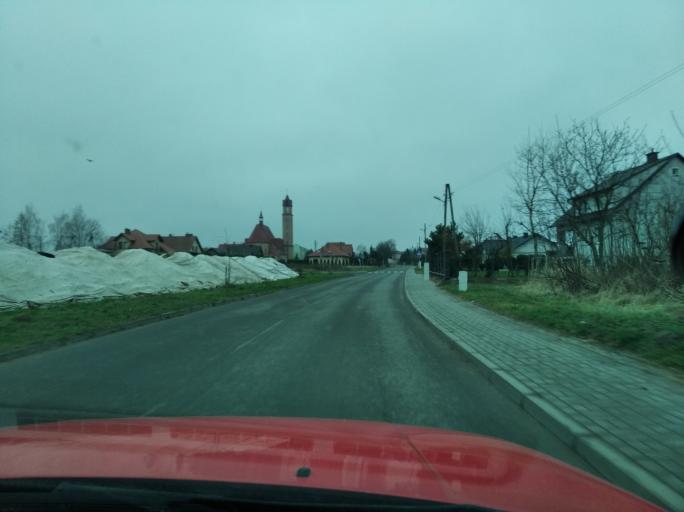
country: PL
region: Subcarpathian Voivodeship
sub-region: Powiat przeworski
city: Przeworsk
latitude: 50.0601
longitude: 22.5125
